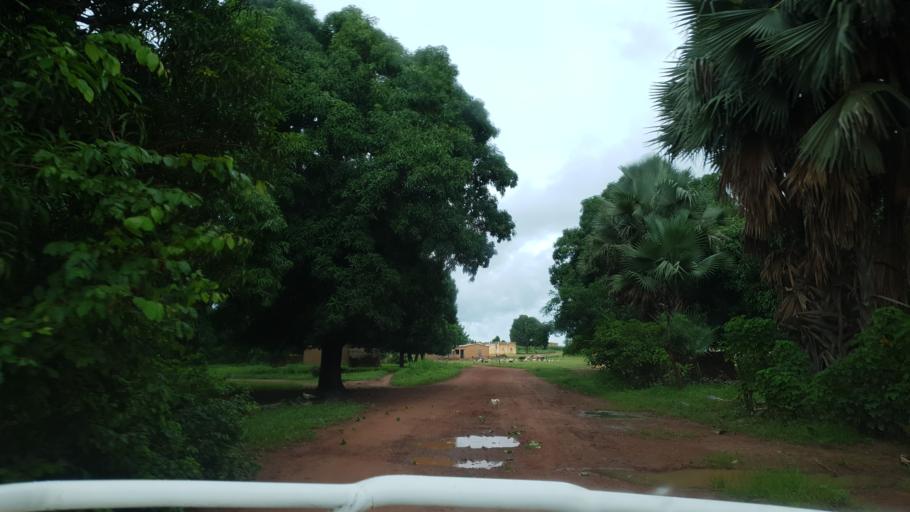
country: ML
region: Sikasso
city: Sikasso
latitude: 11.6746
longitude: -6.1708
